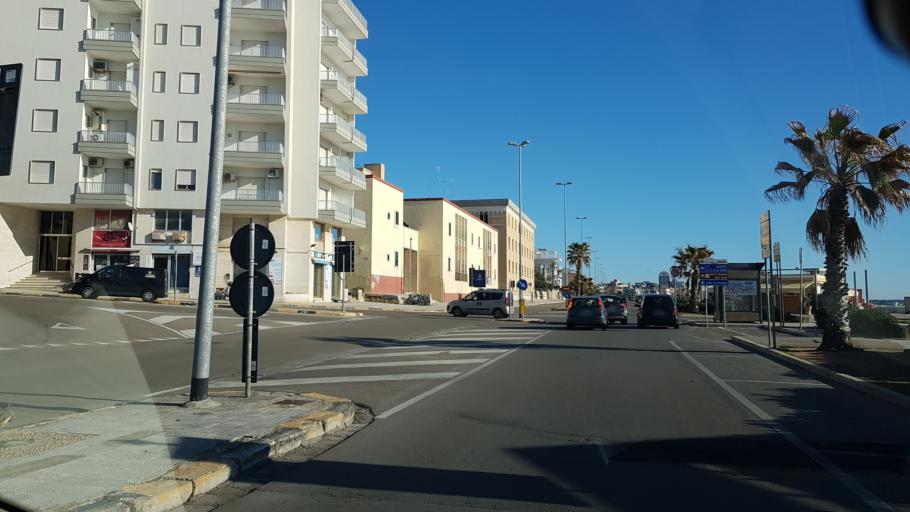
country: IT
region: Apulia
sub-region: Provincia di Lecce
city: Gallipoli
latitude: 40.0531
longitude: 17.9921
